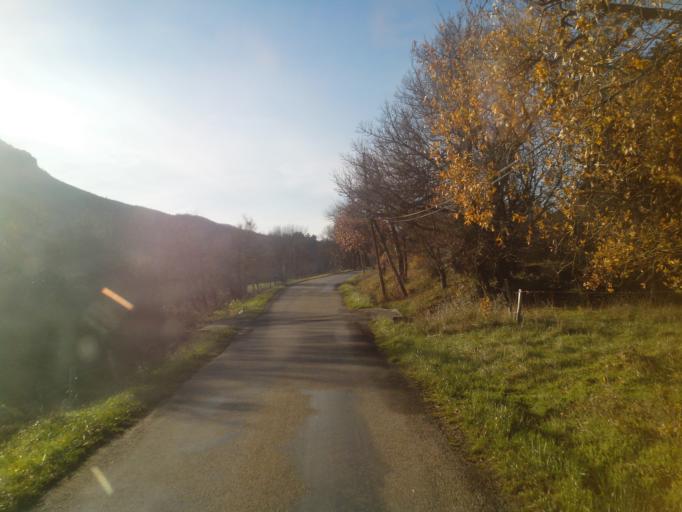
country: FR
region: Languedoc-Roussillon
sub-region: Departement des Pyrenees-Orientales
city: Saint-Paul-de-Fenouillet
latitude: 42.8784
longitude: 2.3936
